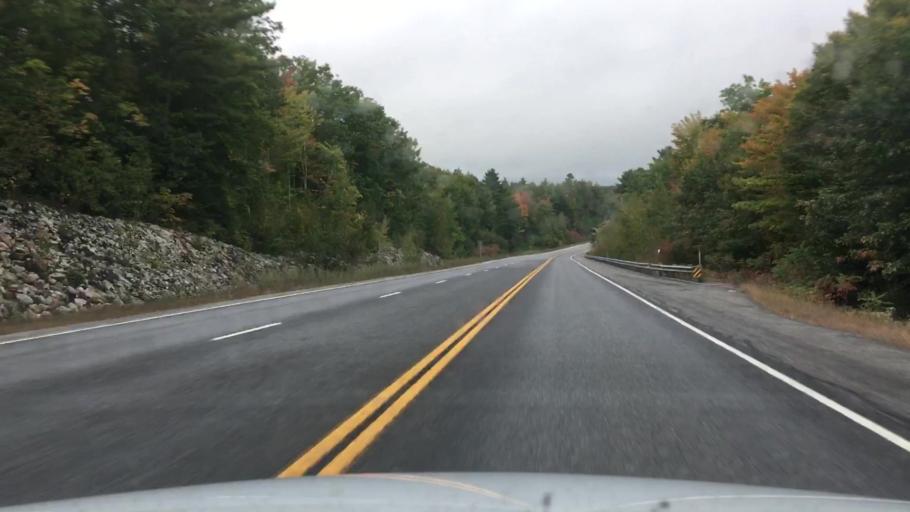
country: US
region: Maine
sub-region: Cumberland County
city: New Gloucester
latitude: 43.9630
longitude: -70.3590
